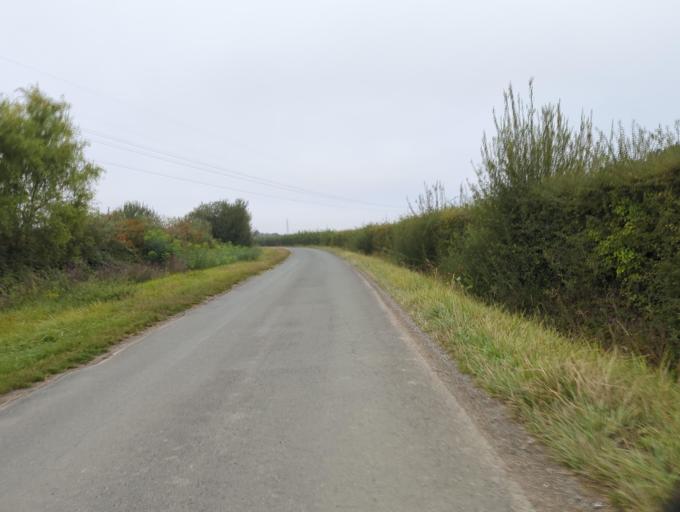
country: FR
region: Pays de la Loire
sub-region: Departement de Maine-et-Loire
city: Trelaze
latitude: 47.4795
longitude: -0.4666
